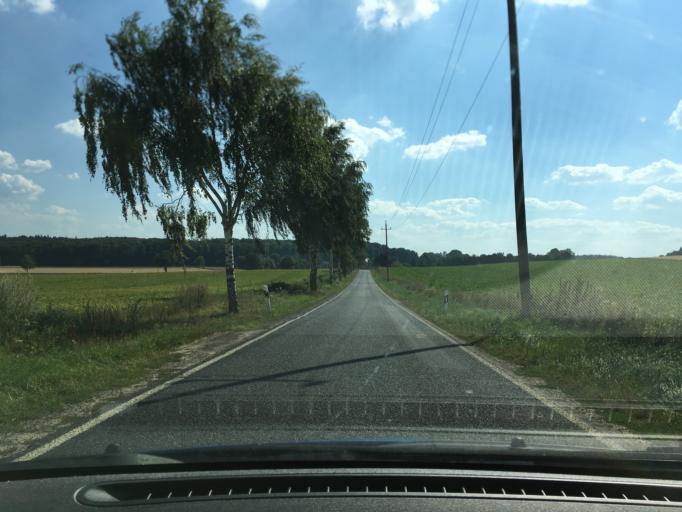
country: DE
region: Lower Saxony
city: Godenstorf
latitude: 53.2025
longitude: 10.1120
